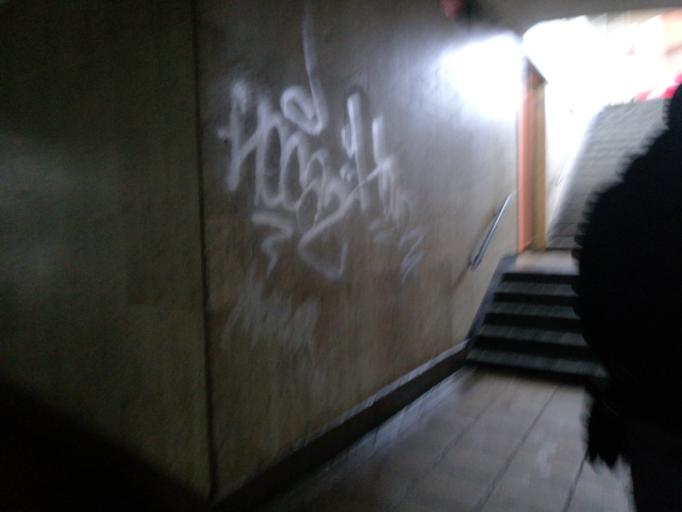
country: RO
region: Brasov
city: Brasov
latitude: 45.6614
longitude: 25.6138
